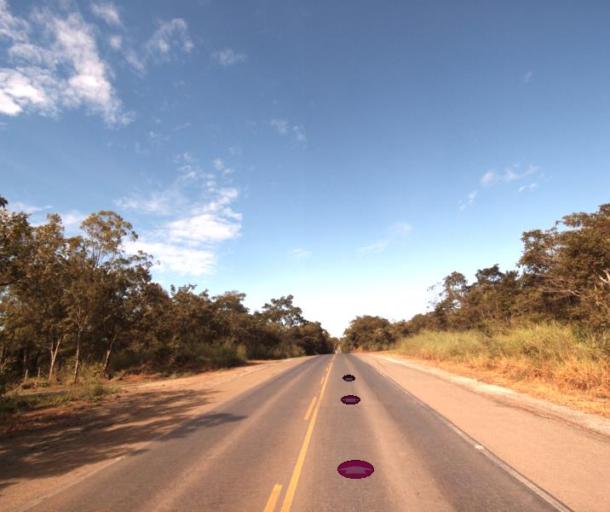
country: BR
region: Goias
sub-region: Itapaci
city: Itapaci
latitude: -14.8132
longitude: -49.2930
